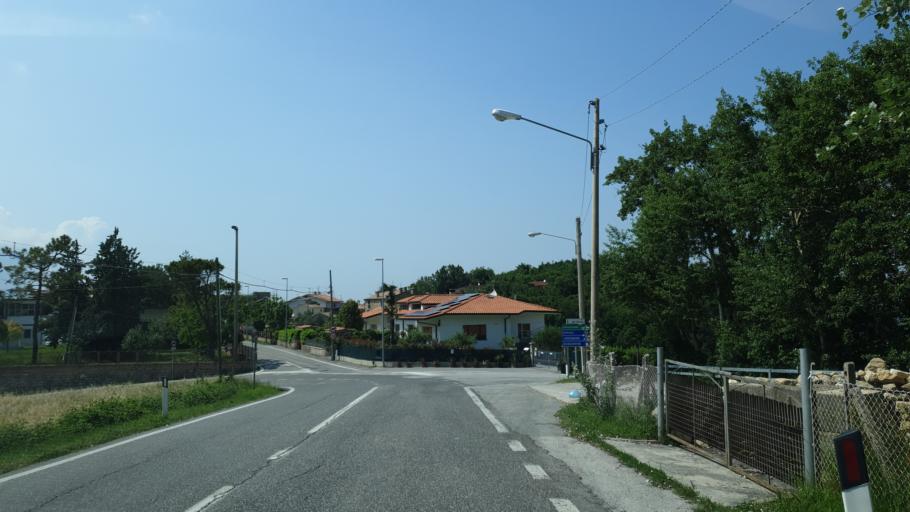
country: SM
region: San Marino
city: San Marino
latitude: 43.9372
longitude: 12.4338
